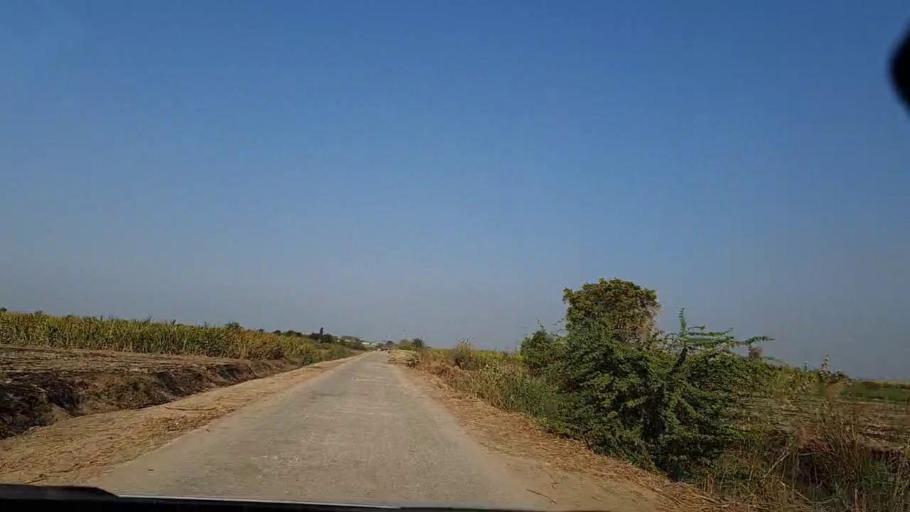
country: PK
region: Sindh
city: Mirwah Gorchani
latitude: 25.2361
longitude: 68.9843
